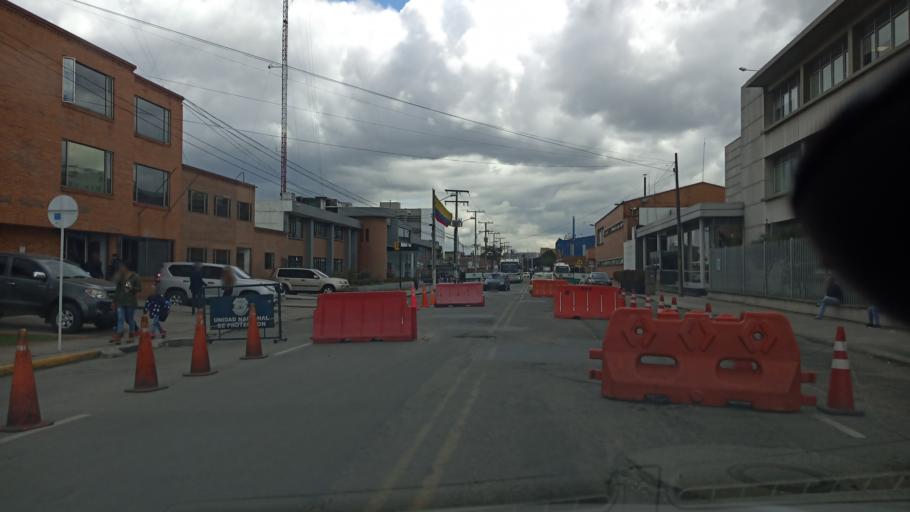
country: CO
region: Bogota D.C.
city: Bogota
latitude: 4.6287
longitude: -74.1134
